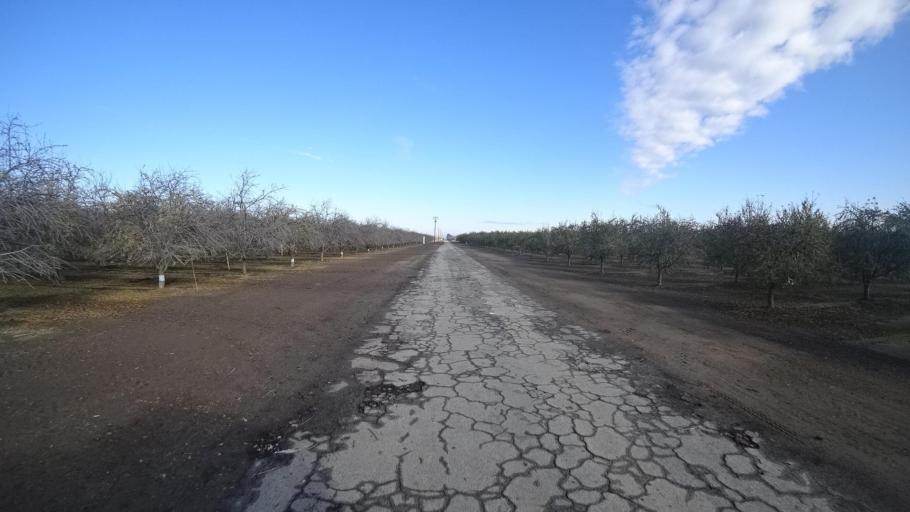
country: US
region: California
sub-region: Kern County
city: McFarland
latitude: 35.7054
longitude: -119.3208
